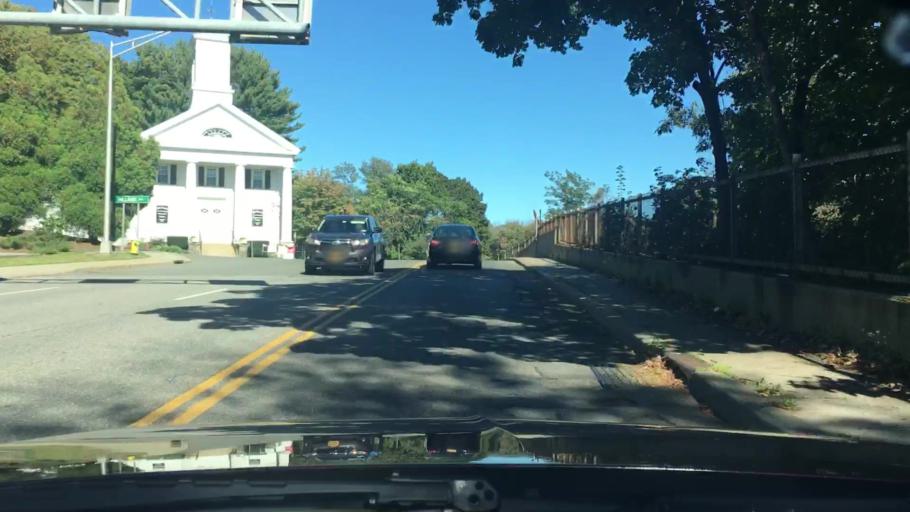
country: US
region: New York
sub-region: Westchester County
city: Mount Kisco
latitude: 41.2099
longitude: -73.7292
